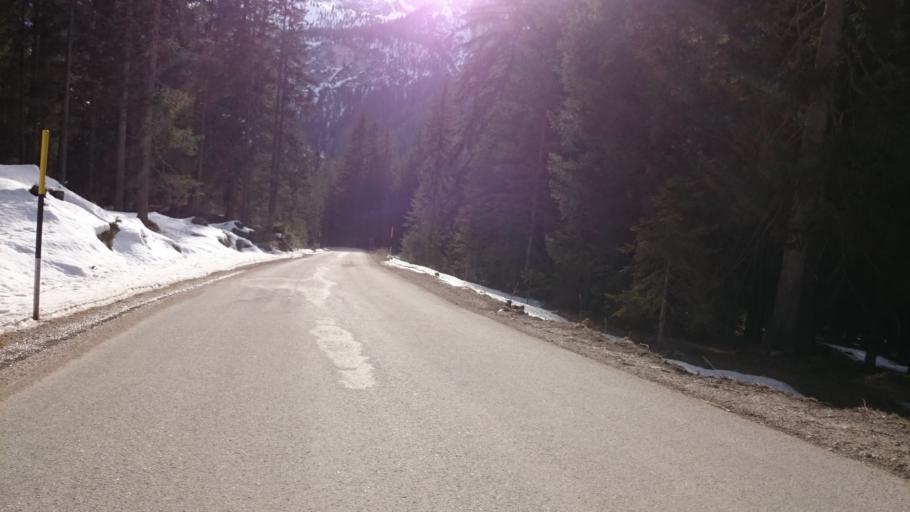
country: IT
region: Trentino-Alto Adige
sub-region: Bolzano
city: Braies
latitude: 46.6728
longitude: 12.1531
